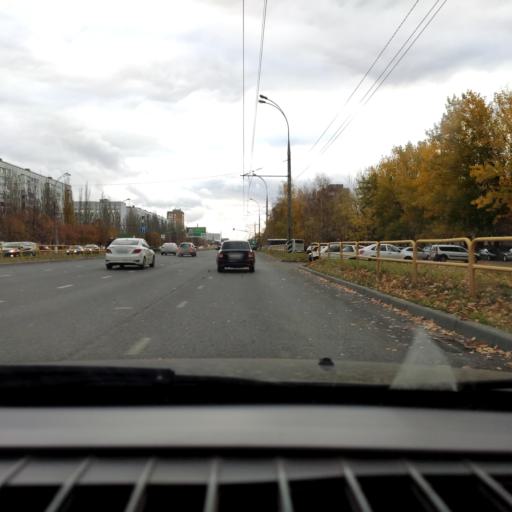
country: RU
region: Samara
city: Tol'yatti
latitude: 53.5132
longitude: 49.2933
